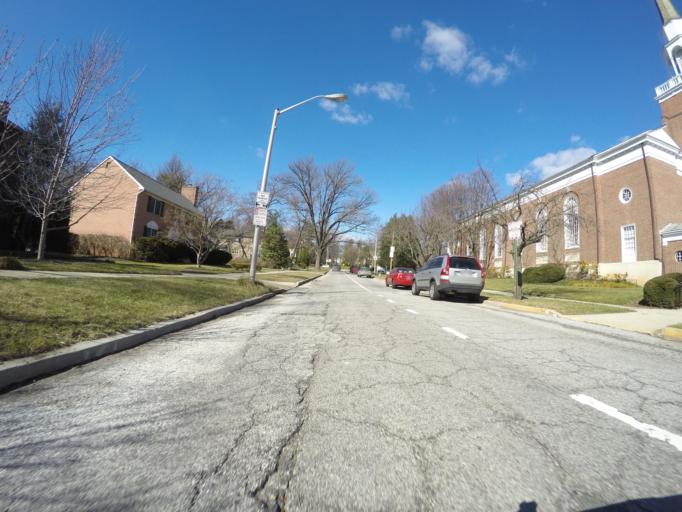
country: US
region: Maryland
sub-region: City of Baltimore
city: Baltimore
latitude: 39.3395
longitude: -76.6185
